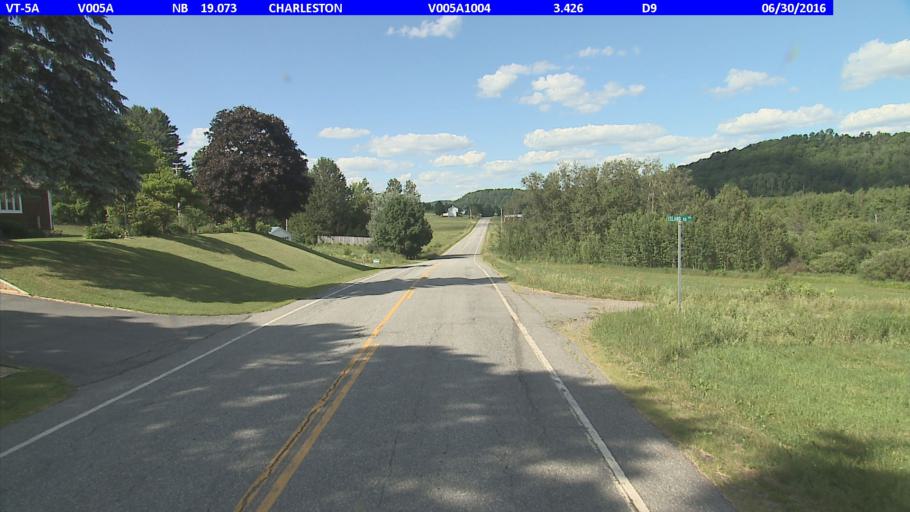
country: US
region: Vermont
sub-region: Orleans County
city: Newport
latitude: 44.8795
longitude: -72.0595
